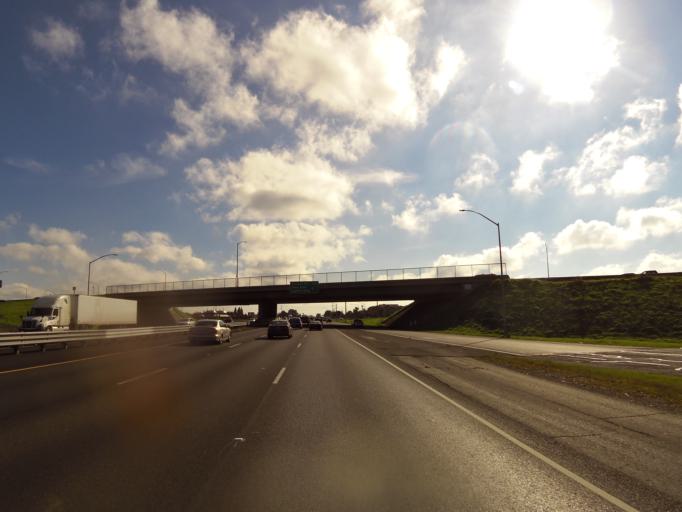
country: US
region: California
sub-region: Sacramento County
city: Florin
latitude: 38.4578
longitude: -121.4112
